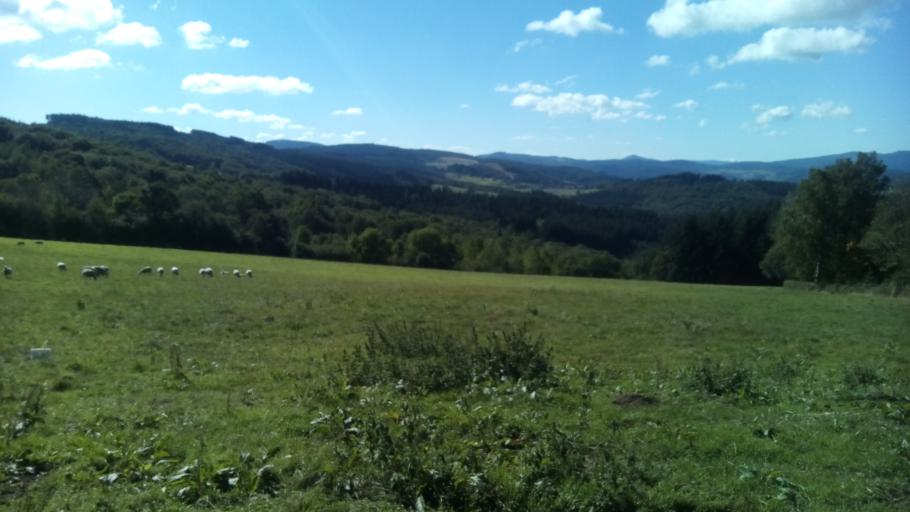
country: FR
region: Bourgogne
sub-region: Departement de Saone-et-Loire
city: La Roche-Vineuse
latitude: 46.2874
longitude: 4.6355
